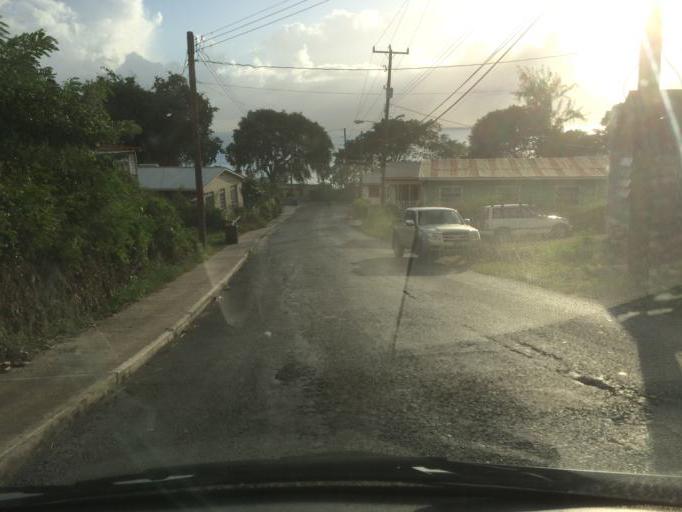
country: BB
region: Saint Lucy
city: Checker Hall
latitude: 13.2804
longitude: -59.6472
